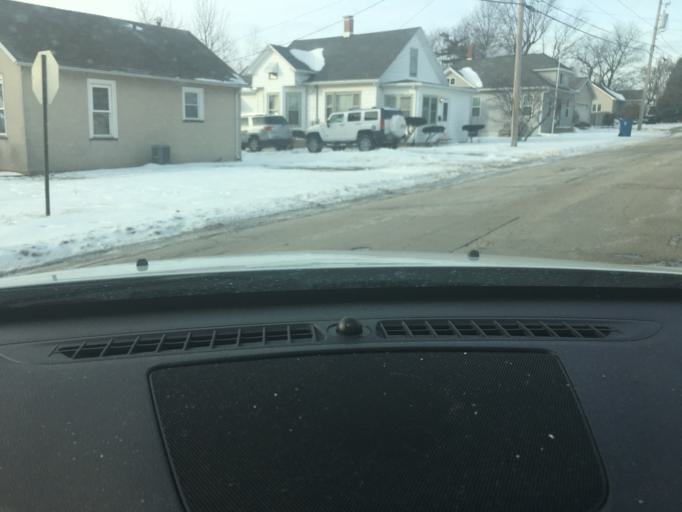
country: US
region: Illinois
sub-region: LaSalle County
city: Peru
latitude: 41.3306
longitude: -89.1132
